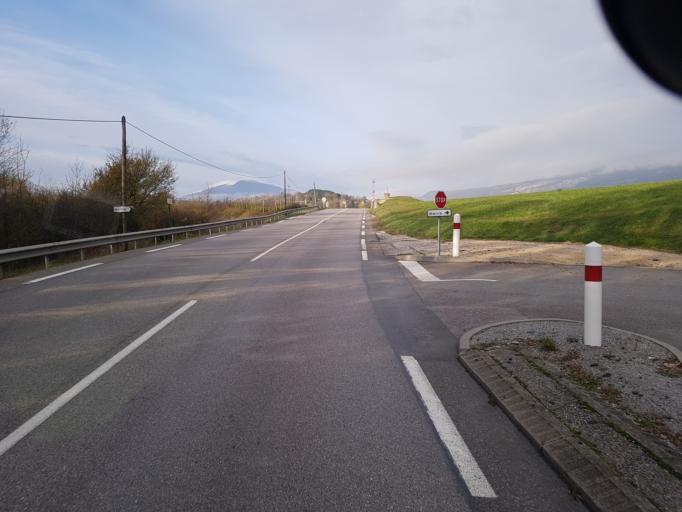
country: FR
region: Rhone-Alpes
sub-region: Departement de la Haute-Savoie
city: Frangy
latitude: 46.0323
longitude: 5.8880
